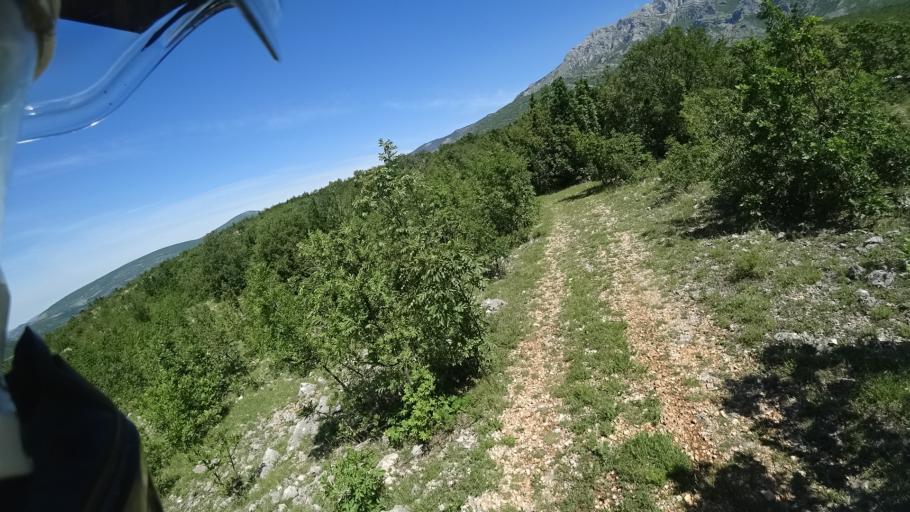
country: BA
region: Federation of Bosnia and Herzegovina
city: Bosansko Grahovo
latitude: 44.0171
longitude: 16.3612
